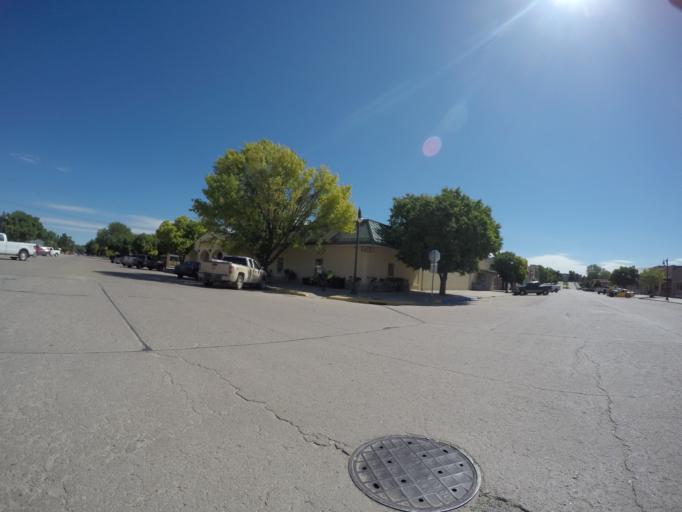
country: US
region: Kansas
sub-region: Rawlins County
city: Atwood
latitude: 39.8078
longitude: -101.0422
